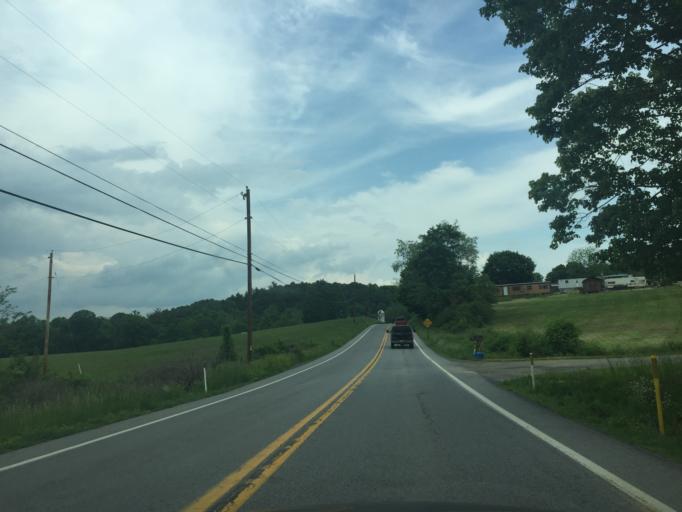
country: US
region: Pennsylvania
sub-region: Fulton County
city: McConnellsburg
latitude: 40.0687
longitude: -77.9343
